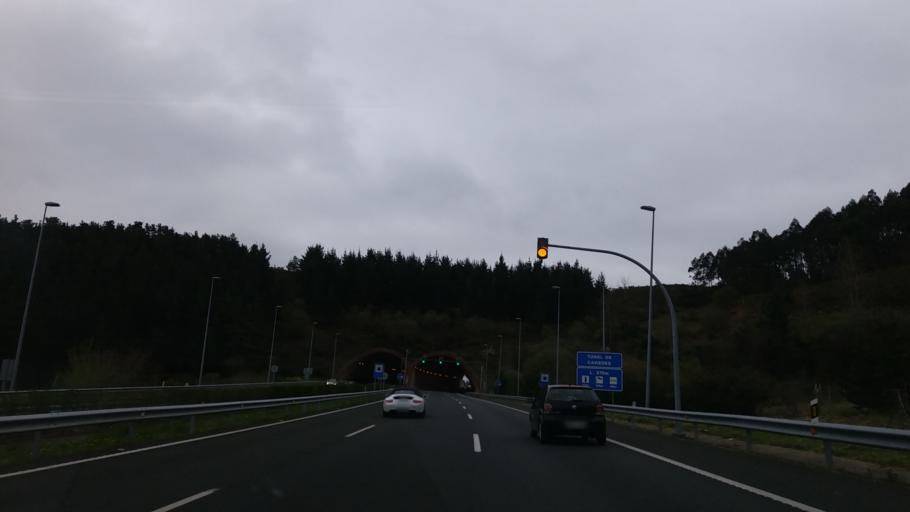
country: ES
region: Cantabria
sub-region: Provincia de Cantabria
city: Comillas
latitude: 43.3330
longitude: -4.3240
